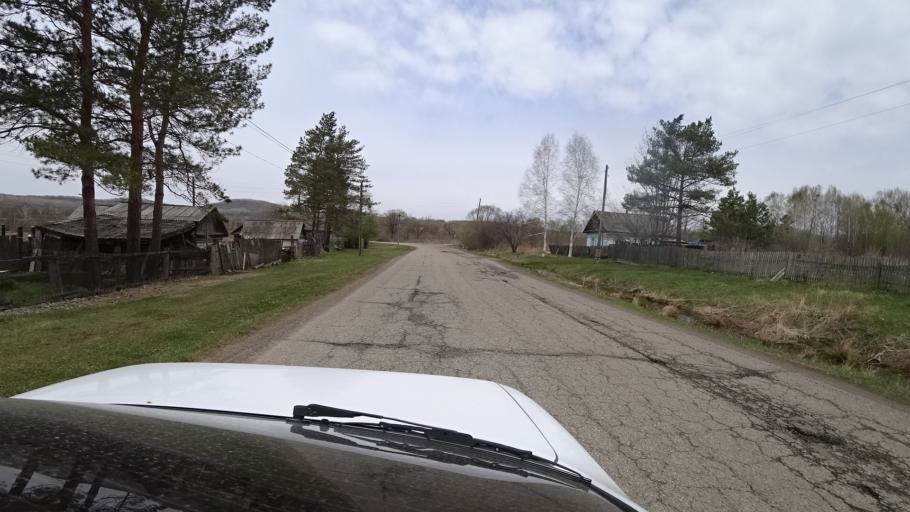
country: RU
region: Primorskiy
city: Dal'nerechensk
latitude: 45.7953
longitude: 134.1071
